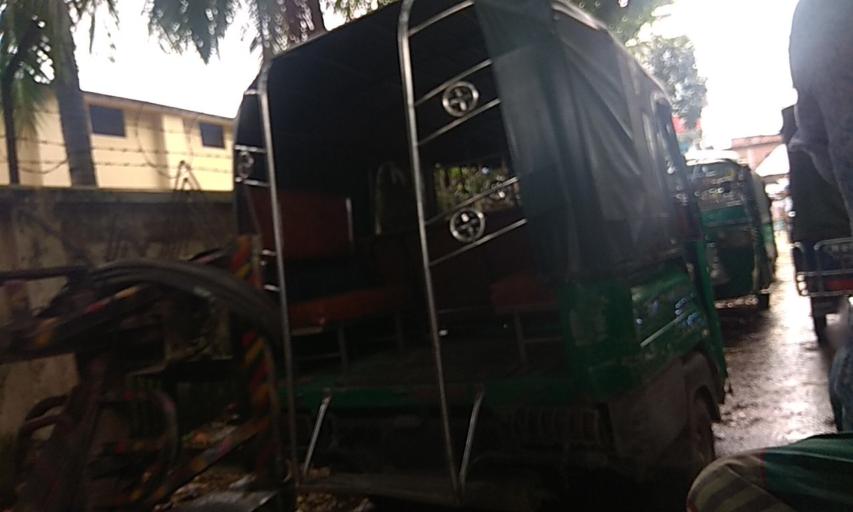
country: BD
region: Dhaka
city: Dohar
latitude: 23.4763
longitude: 90.0265
